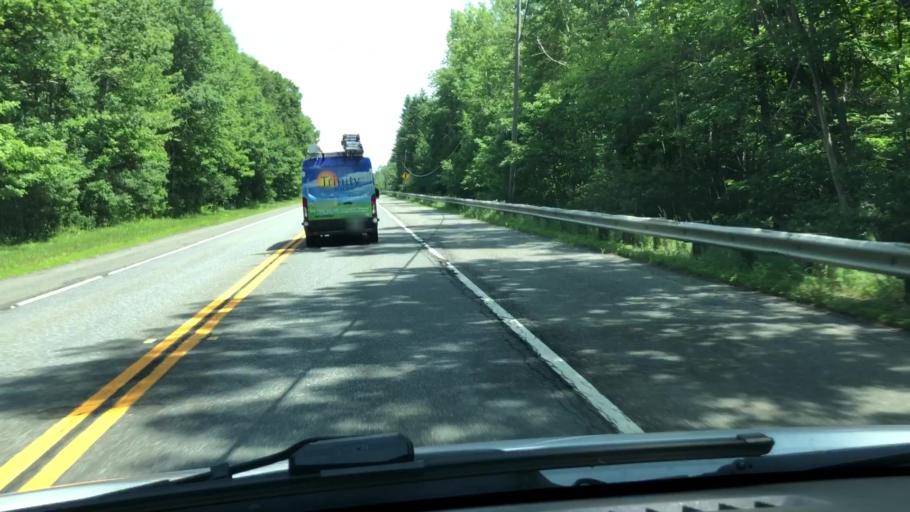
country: US
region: Massachusetts
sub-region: Berkshire County
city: Hinsdale
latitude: 42.4957
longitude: -73.0056
